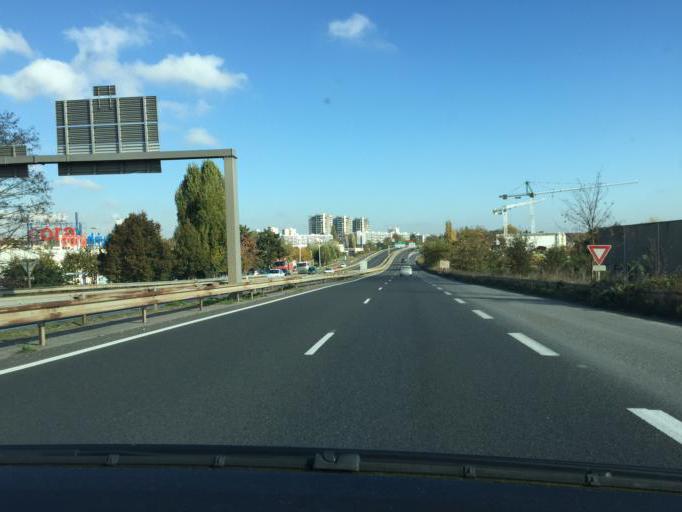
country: FR
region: Ile-de-France
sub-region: Departement de l'Essonne
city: Massy
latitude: 48.7228
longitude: 2.2768
